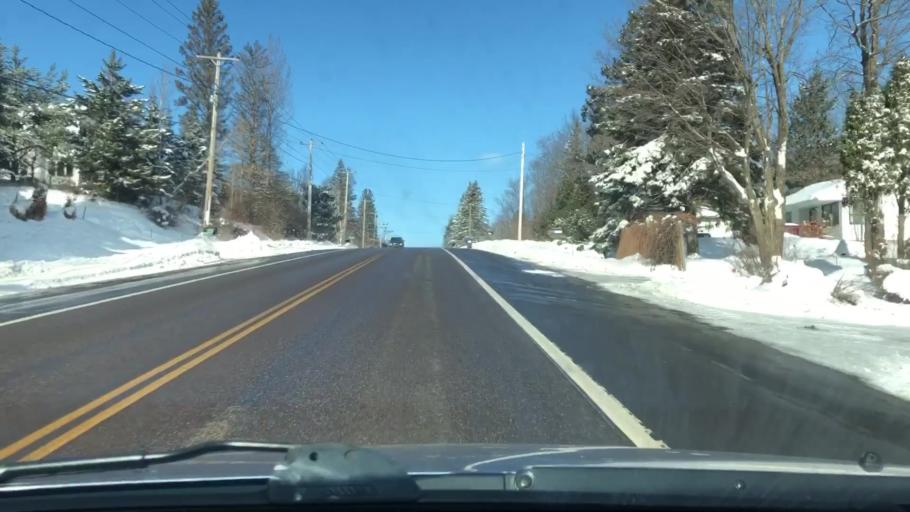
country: US
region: Minnesota
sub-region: Saint Louis County
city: Duluth
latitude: 46.8119
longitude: -92.1322
